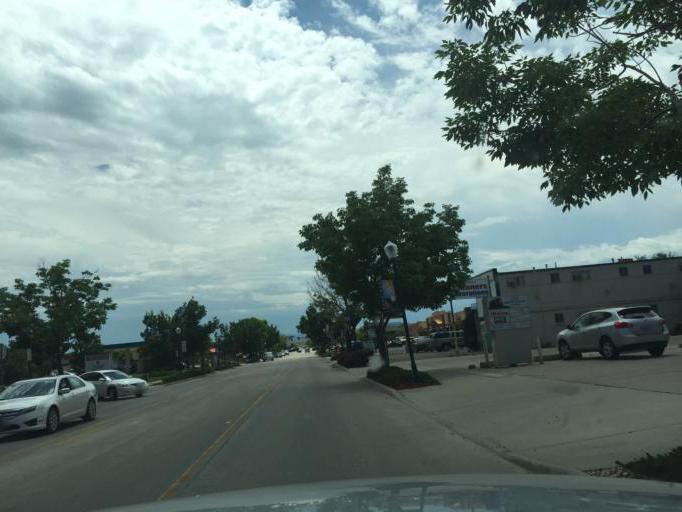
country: US
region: Colorado
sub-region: Douglas County
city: Castle Rock
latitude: 39.3680
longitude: -104.8608
